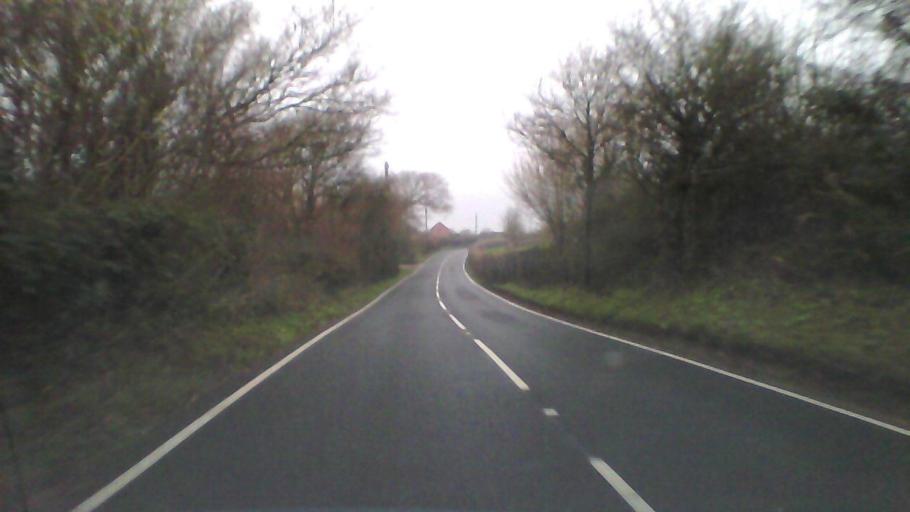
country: GB
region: England
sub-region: Isle of Wight
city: Newport
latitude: 50.6956
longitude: -1.2643
